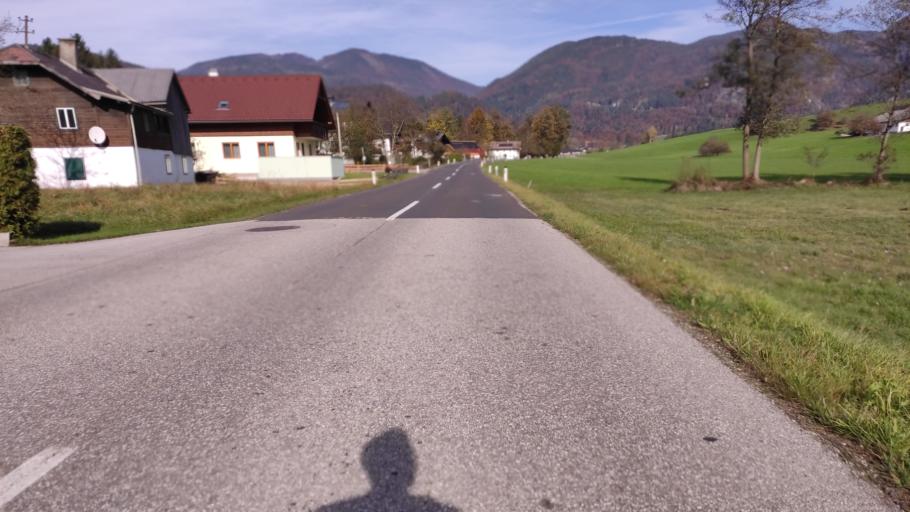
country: AT
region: Salzburg
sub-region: Politischer Bezirk Salzburg-Umgebung
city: Strobl
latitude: 47.7239
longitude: 13.5123
